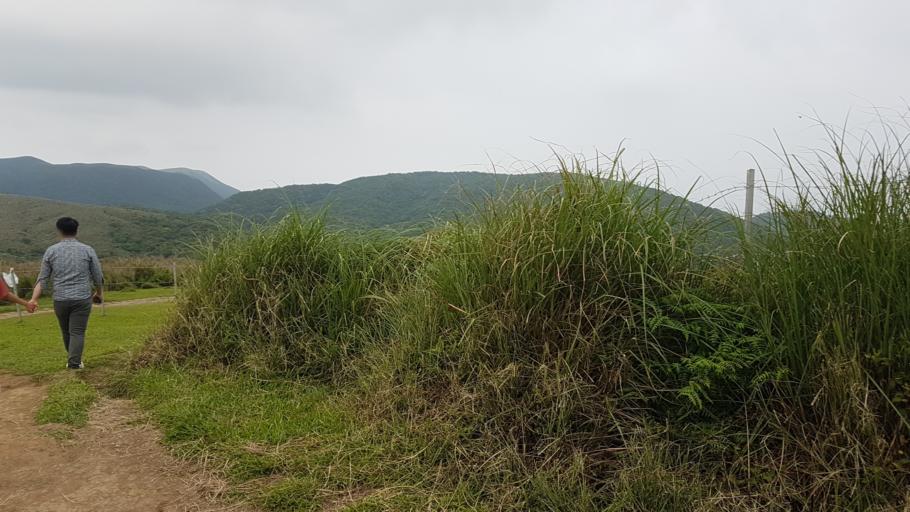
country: TW
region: Taipei
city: Taipei
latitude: 25.1604
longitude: 121.5748
